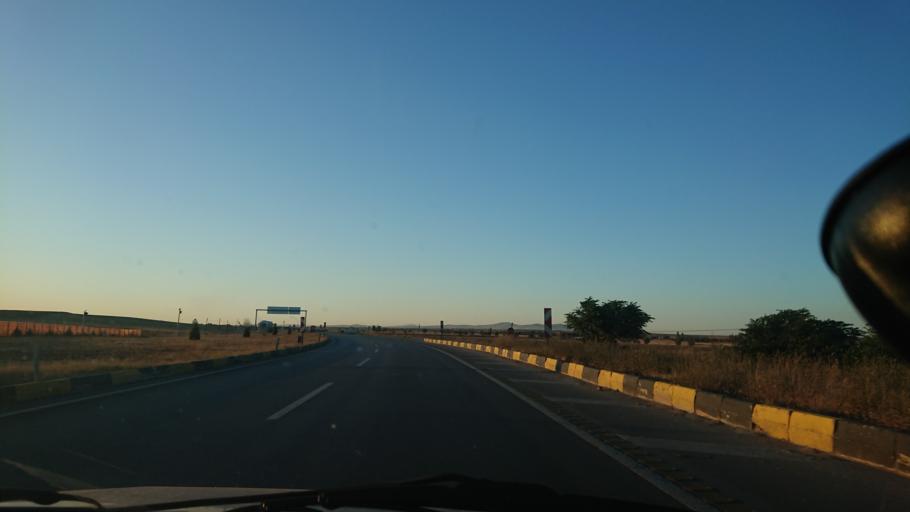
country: TR
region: Eskisehir
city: Mahmudiye
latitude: 39.5184
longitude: 30.9622
